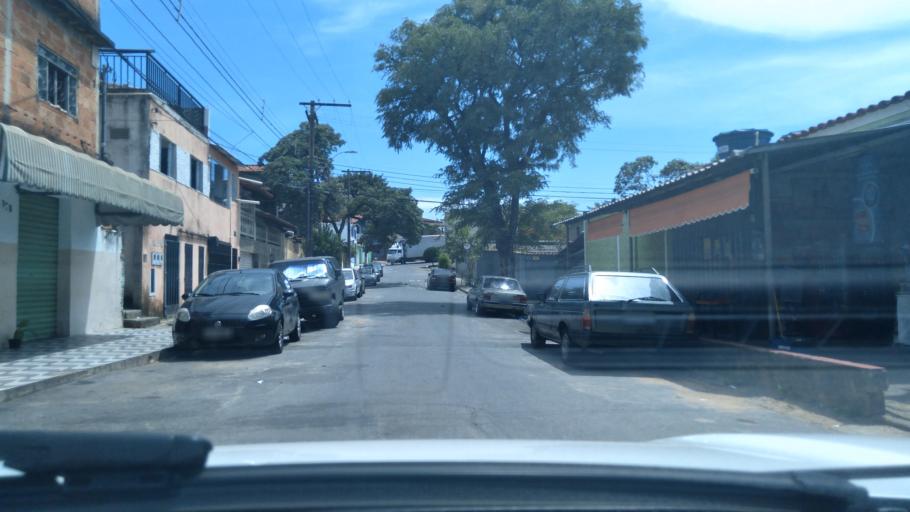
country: BR
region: Minas Gerais
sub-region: Contagem
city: Contagem
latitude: -19.9207
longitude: -43.9994
